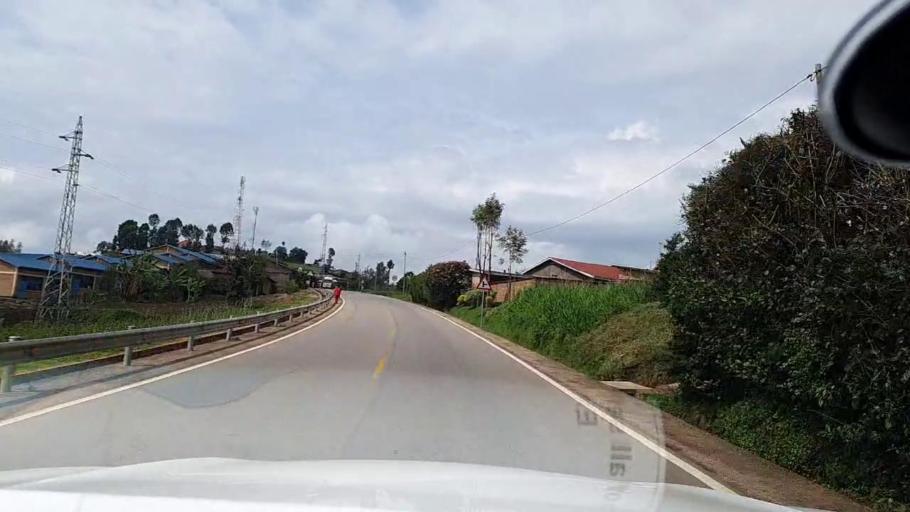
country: RW
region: Southern Province
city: Nzega
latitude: -2.4831
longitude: 29.5332
